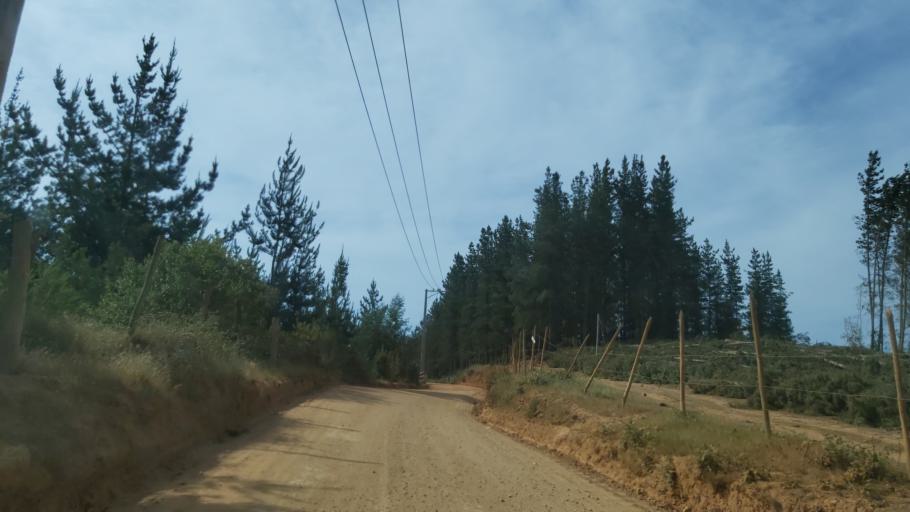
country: CL
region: Maule
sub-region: Provincia de Talca
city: Constitucion
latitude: -34.8498
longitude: -72.0336
